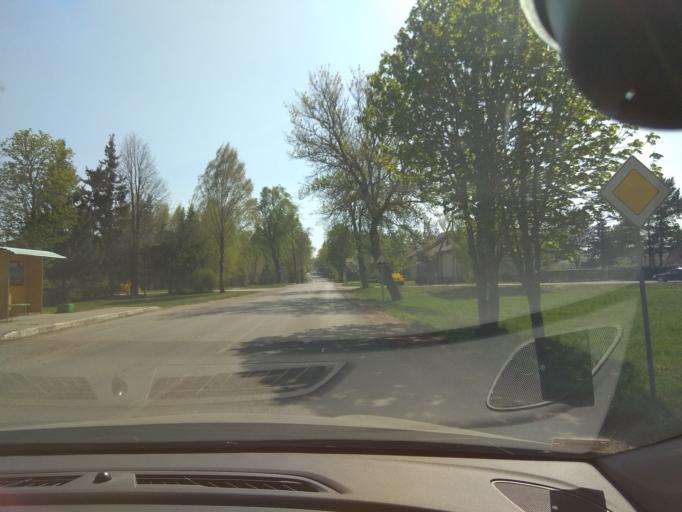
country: LT
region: Panevezys
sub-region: Panevezys City
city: Panevezys
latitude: 55.9041
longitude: 24.2373
